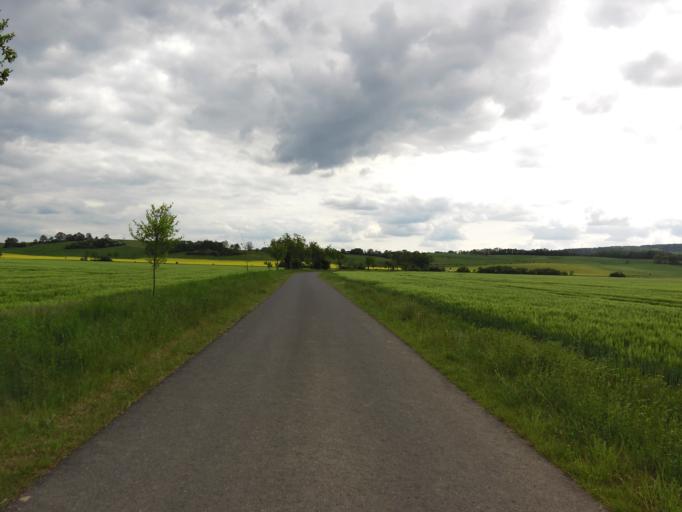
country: DE
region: Thuringia
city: Creuzburg
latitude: 51.0390
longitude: 10.2468
